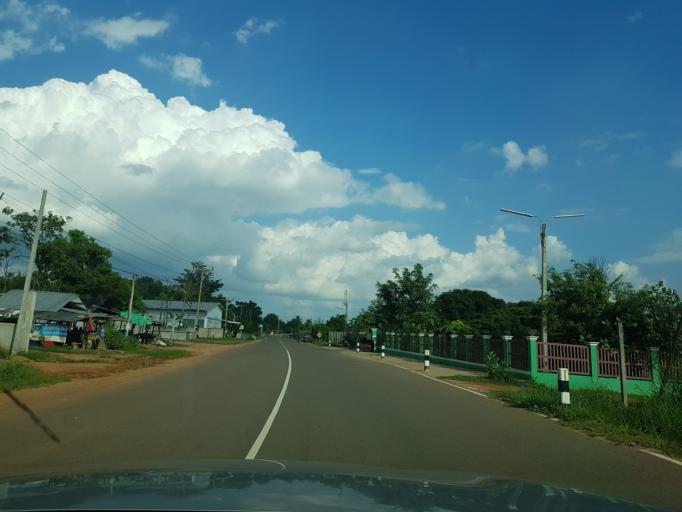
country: TH
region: Nong Khai
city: Pho Tak
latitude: 17.9834
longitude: 102.4440
